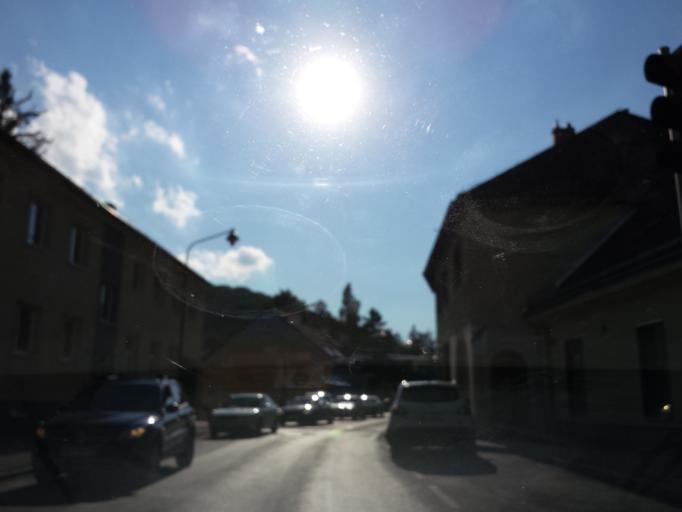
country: AT
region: Lower Austria
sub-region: Politischer Bezirk Modling
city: Perchtoldsdorf
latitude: 48.1376
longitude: 16.2447
